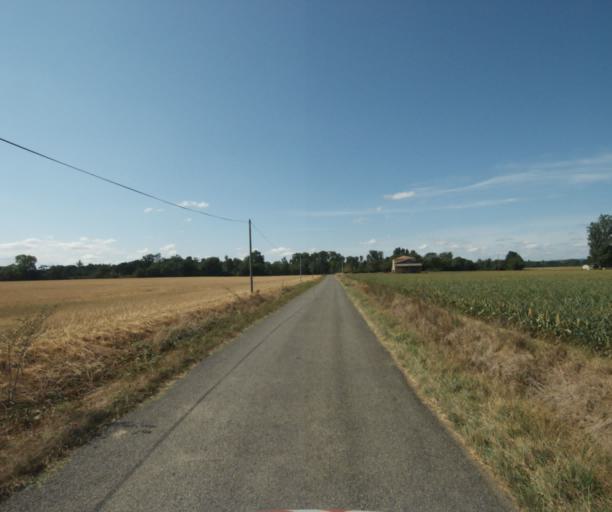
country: FR
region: Midi-Pyrenees
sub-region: Departement de la Haute-Garonne
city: Revel
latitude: 43.4790
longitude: 1.9742
